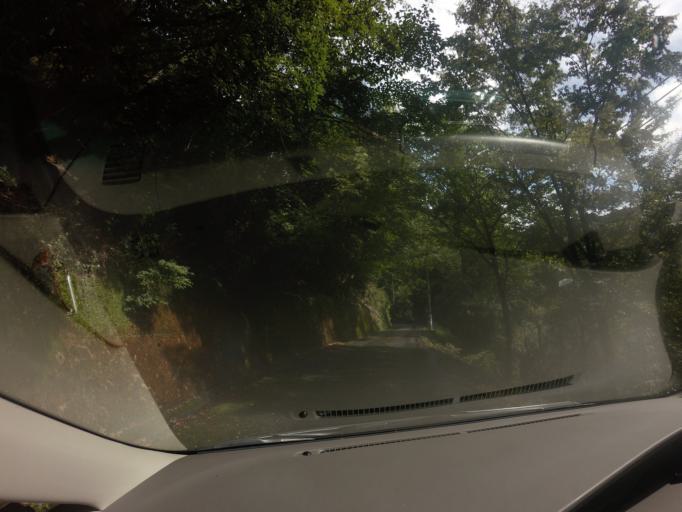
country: JP
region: Wakayama
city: Shingu
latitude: 33.9620
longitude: 135.8580
